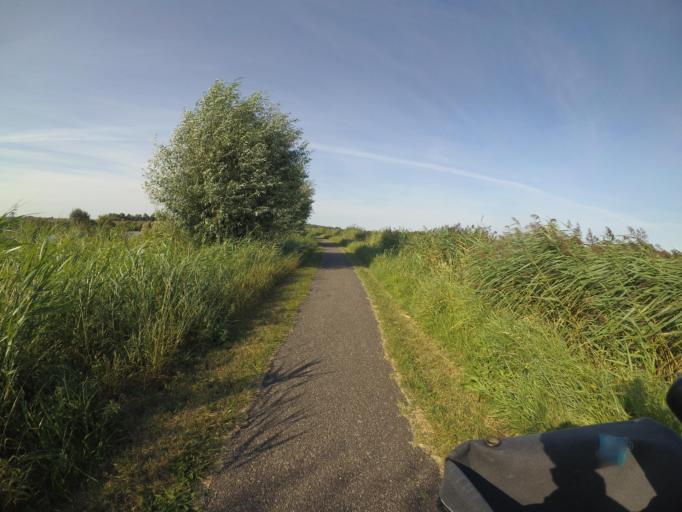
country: NL
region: Friesland
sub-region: Gemeente Dantumadiel
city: Rinsumageast
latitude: 53.3216
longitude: 5.9549
